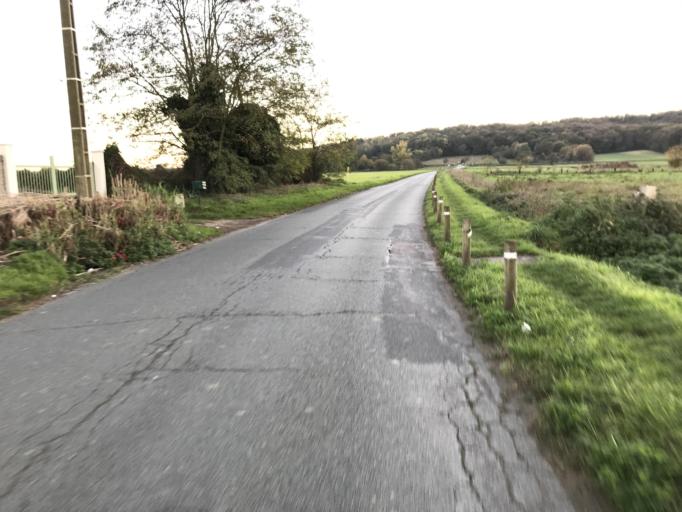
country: FR
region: Ile-de-France
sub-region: Departement de l'Essonne
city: Saulx-les-Chartreux
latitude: 48.6816
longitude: 2.2779
